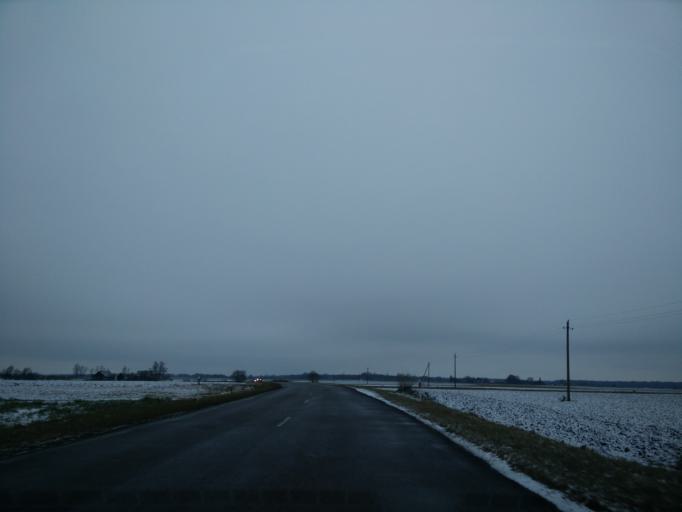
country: LT
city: Ariogala
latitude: 55.3748
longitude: 23.3576
